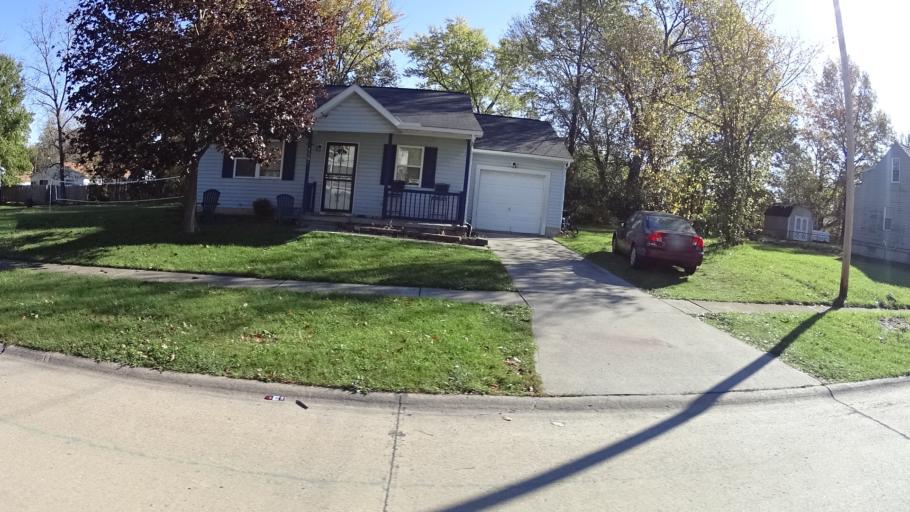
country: US
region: Ohio
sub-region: Lorain County
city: Lorain
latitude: 41.4351
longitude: -82.1563
